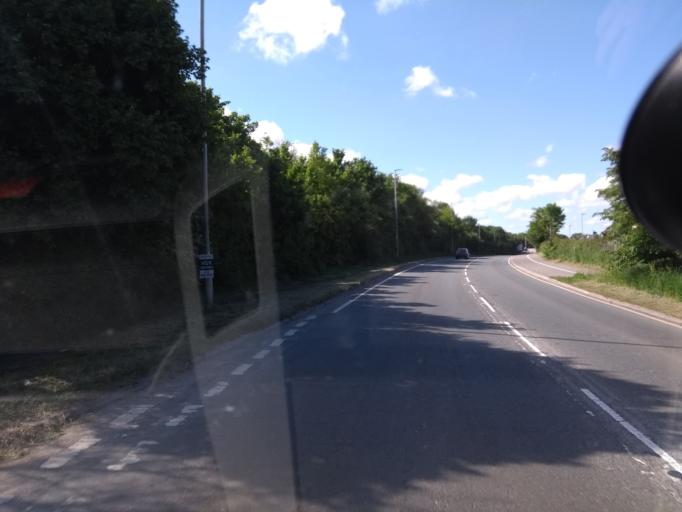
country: GB
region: England
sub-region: Somerset
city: Bridgwater
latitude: 51.1078
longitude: -2.9941
